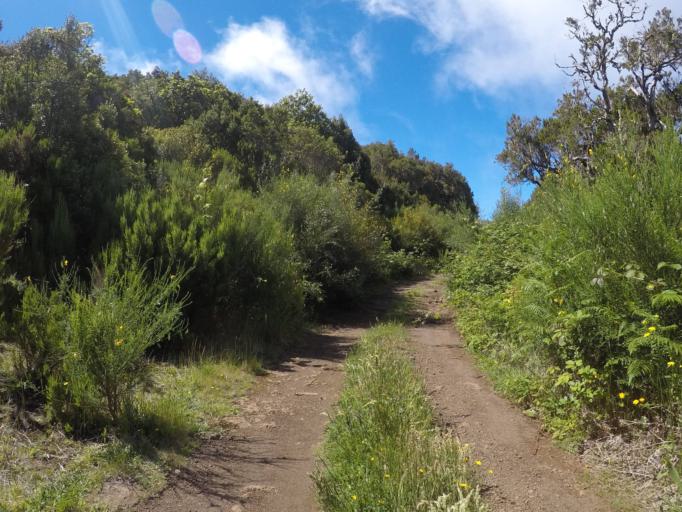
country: PT
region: Madeira
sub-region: Sao Vicente
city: Sao Vicente
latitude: 32.7702
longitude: -17.0593
